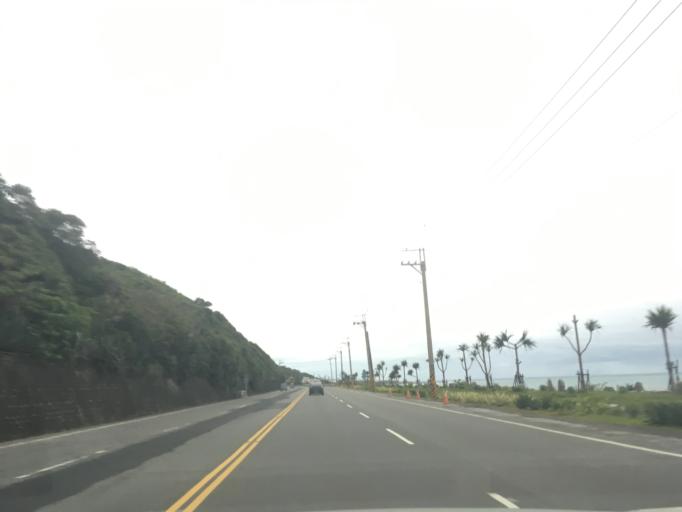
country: TW
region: Taiwan
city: Hengchun
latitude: 22.3459
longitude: 120.8990
